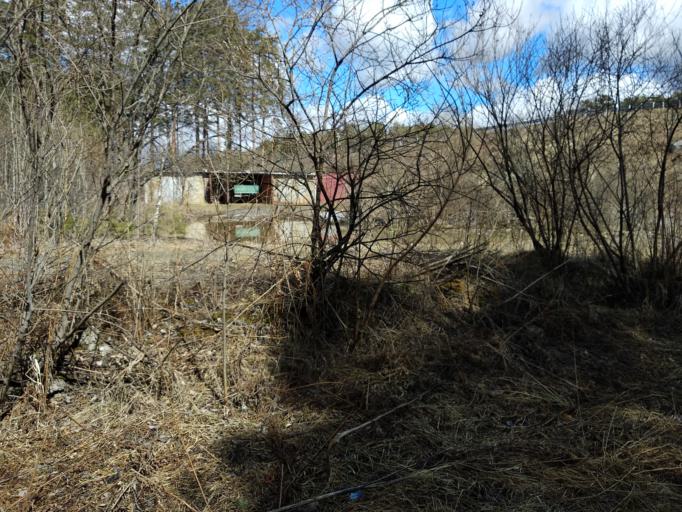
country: RU
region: Sverdlovsk
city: Beryozovsky
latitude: 56.9039
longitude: 60.7560
